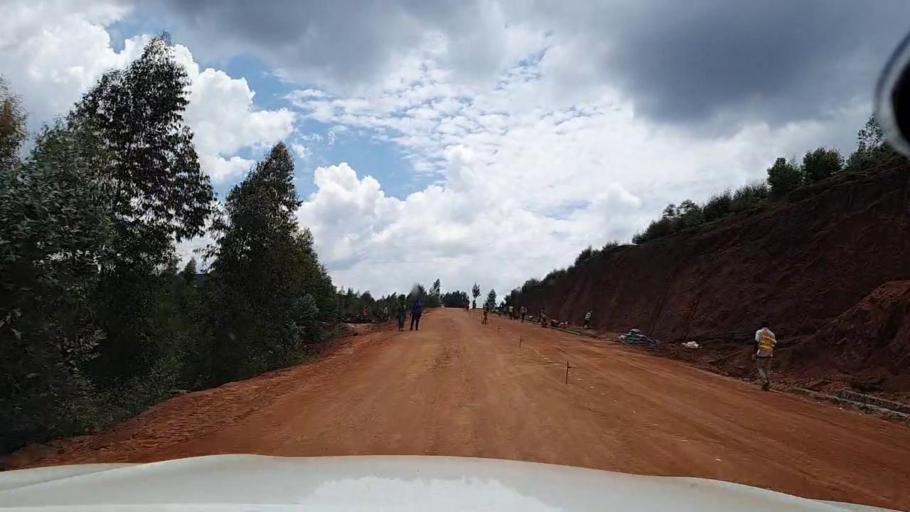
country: RW
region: Southern Province
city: Butare
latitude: -2.7007
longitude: 29.5546
